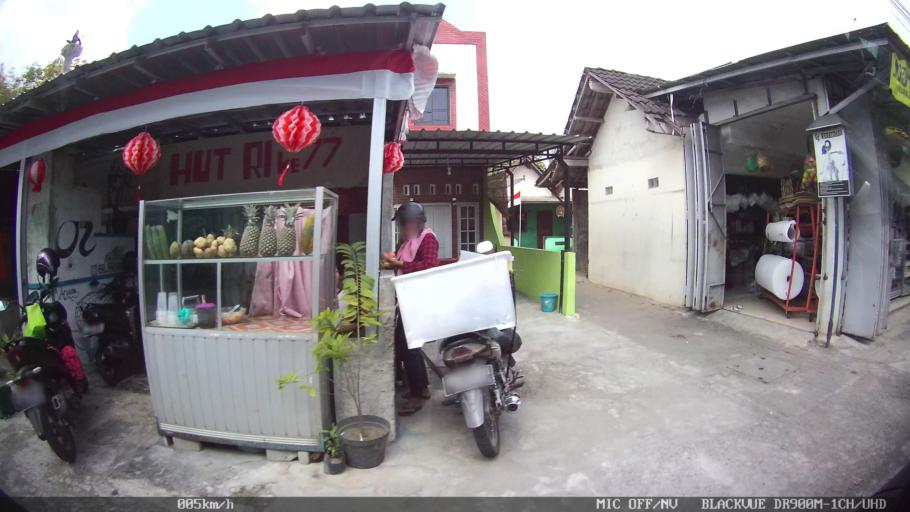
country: ID
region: Daerah Istimewa Yogyakarta
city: Gamping Lor
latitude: -7.8003
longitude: 110.3337
